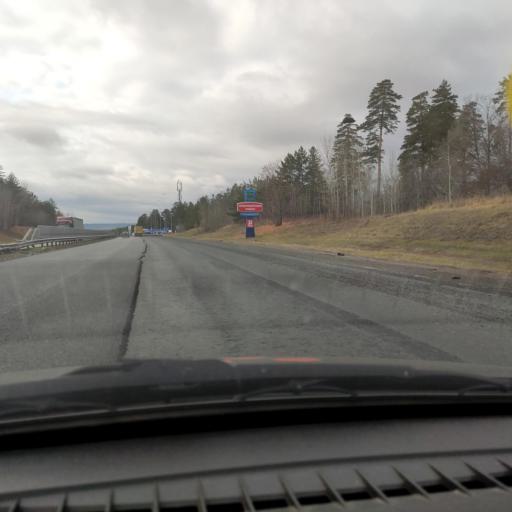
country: RU
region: Samara
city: Kurumoch
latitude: 53.4969
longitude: 50.0842
